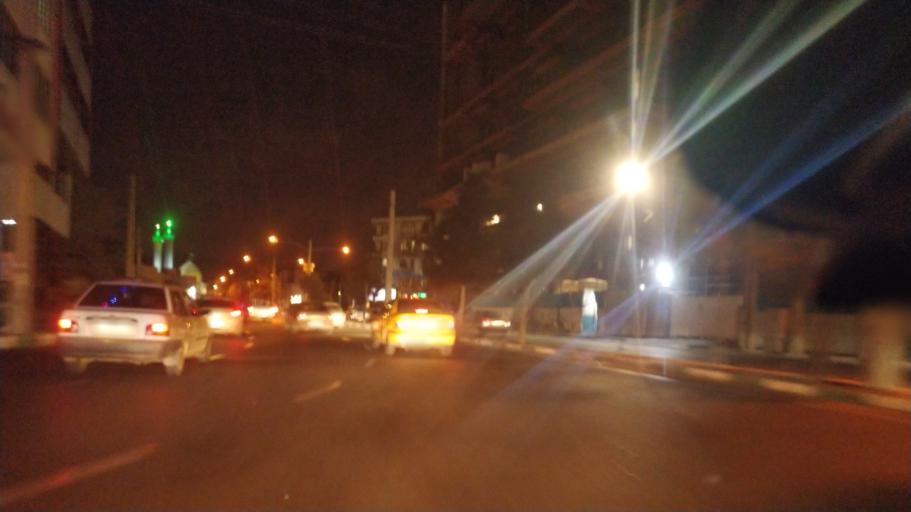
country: IR
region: Alborz
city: Karaj
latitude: 35.8108
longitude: 50.9989
